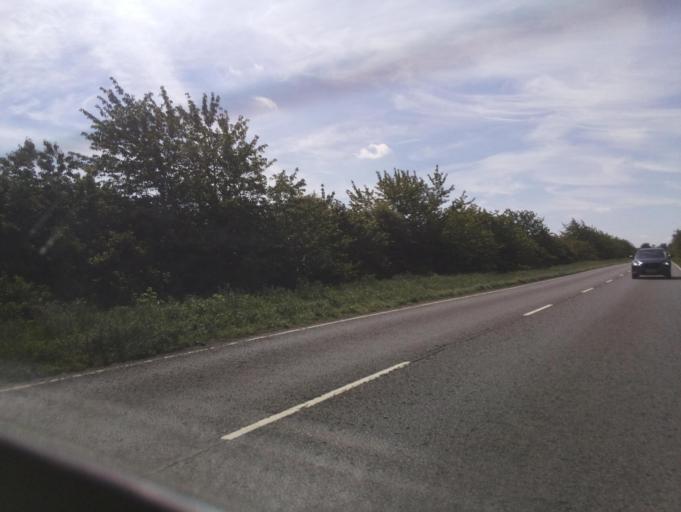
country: GB
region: England
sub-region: North Lincolnshire
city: Kirton in Lindsey
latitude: 53.3776
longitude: -0.5466
